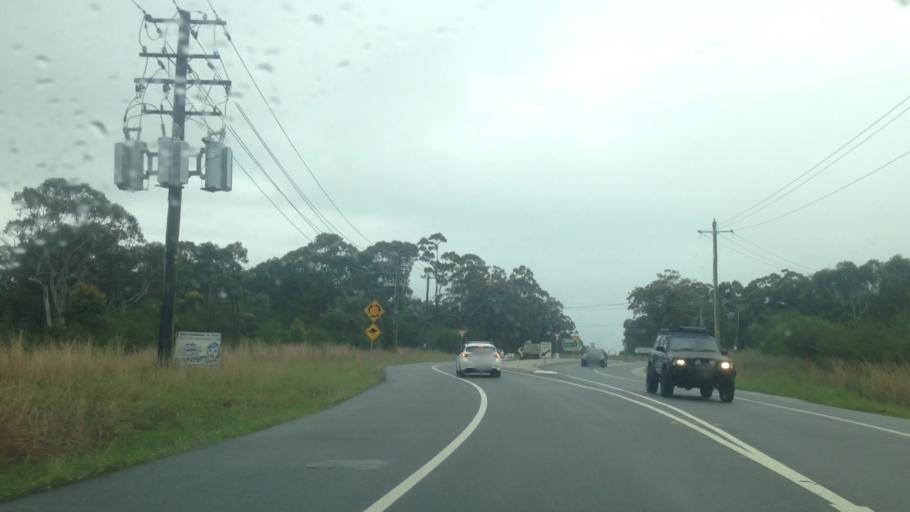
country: AU
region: New South Wales
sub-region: Wyong Shire
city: Charmhaven
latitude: -33.1575
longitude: 151.4787
